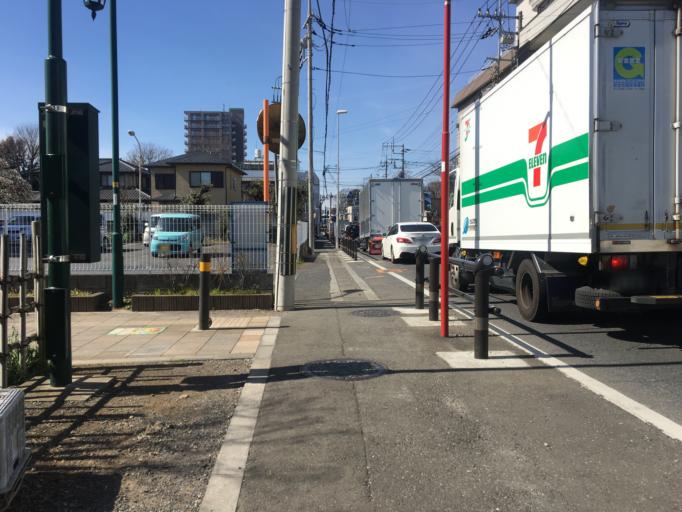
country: JP
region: Saitama
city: Shiki
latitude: 35.8027
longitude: 139.5654
